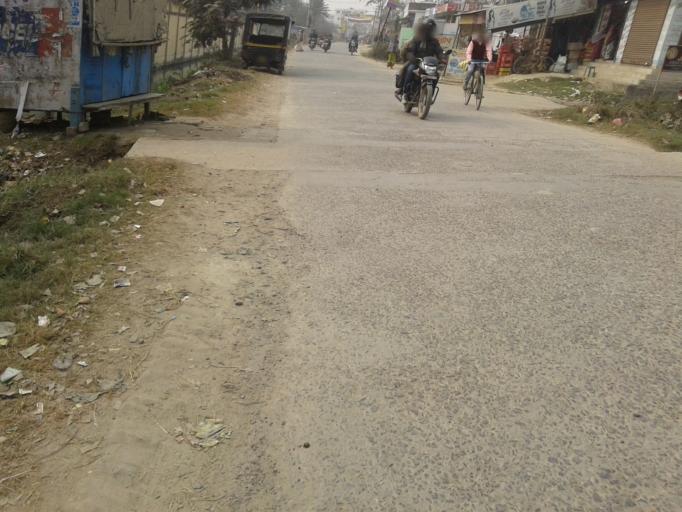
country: IN
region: Bihar
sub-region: Muzaffarpur
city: Muzaffarpur
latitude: 26.1021
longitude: 85.4079
